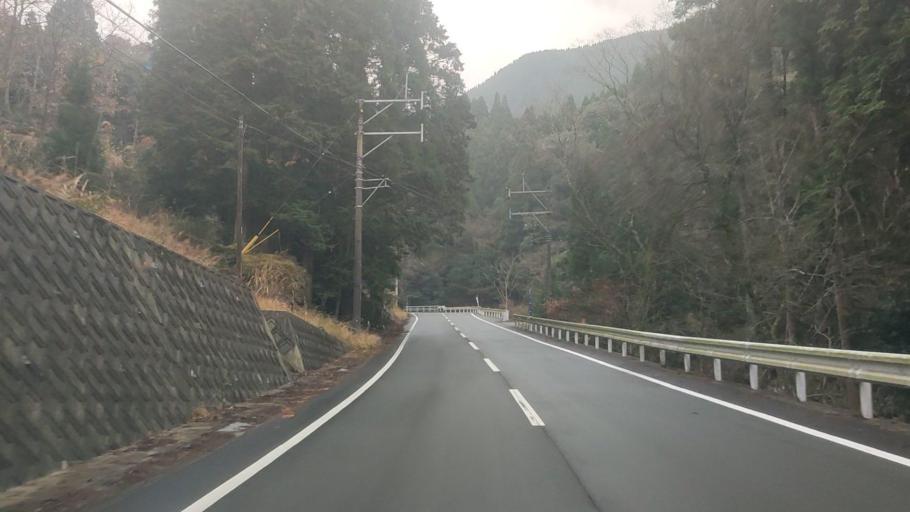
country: JP
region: Kumamoto
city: Matsubase
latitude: 32.5927
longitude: 130.8873
